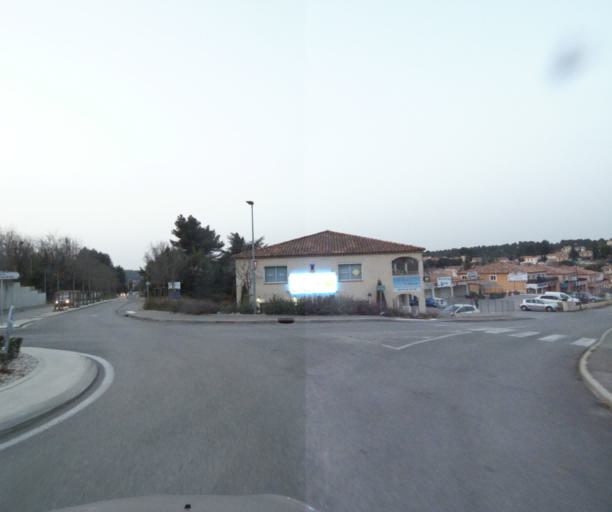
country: FR
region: Provence-Alpes-Cote d'Azur
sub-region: Departement des Bouches-du-Rhone
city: Gardanne
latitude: 43.4285
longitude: 5.4718
